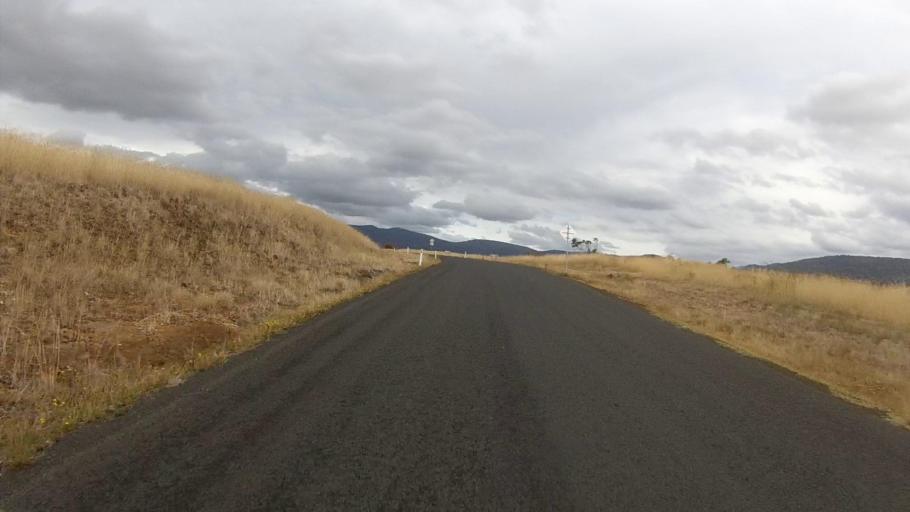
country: AU
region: Tasmania
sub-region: Northern Midlands
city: Evandale
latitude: -41.8180
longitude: 147.7542
